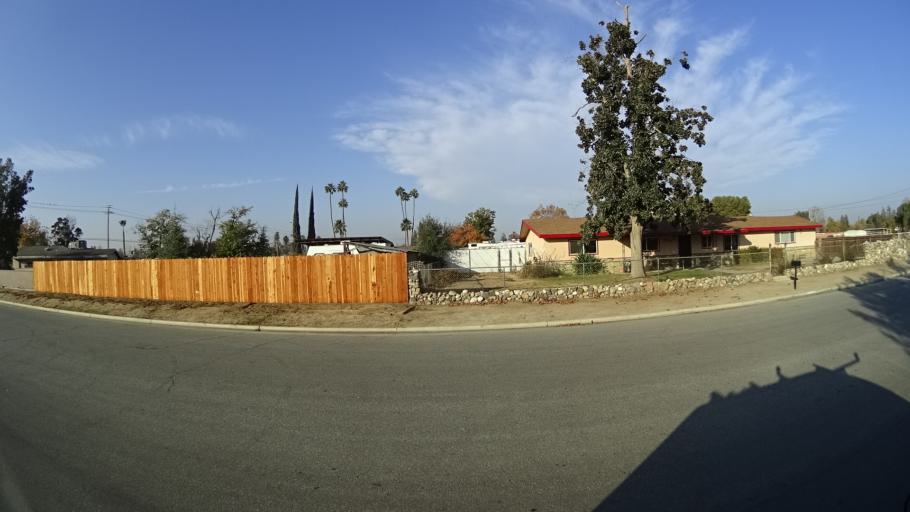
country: US
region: California
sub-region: Kern County
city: Greenacres
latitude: 35.3792
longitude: -119.1189
